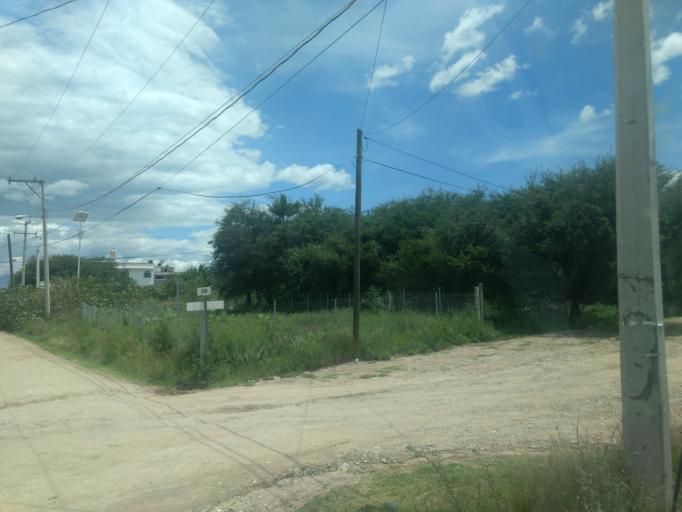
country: MX
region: Oaxaca
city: Ciudad de Huajuapam de Leon
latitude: 17.8153
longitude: -97.7927
